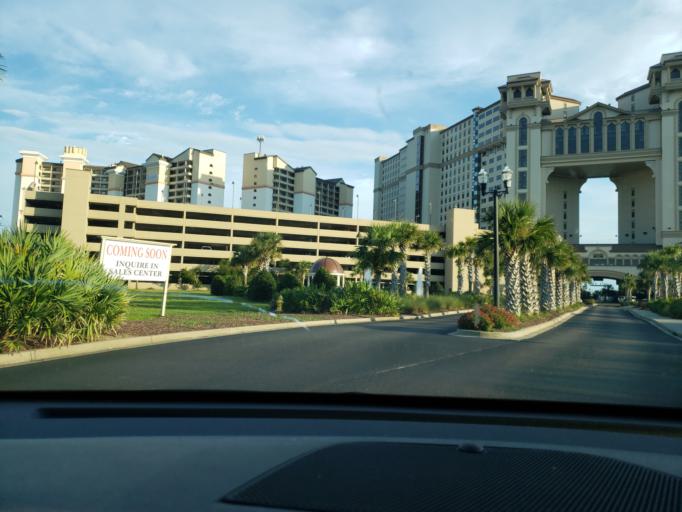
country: US
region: South Carolina
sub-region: Horry County
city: North Myrtle Beach
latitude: 33.7922
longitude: -78.7364
